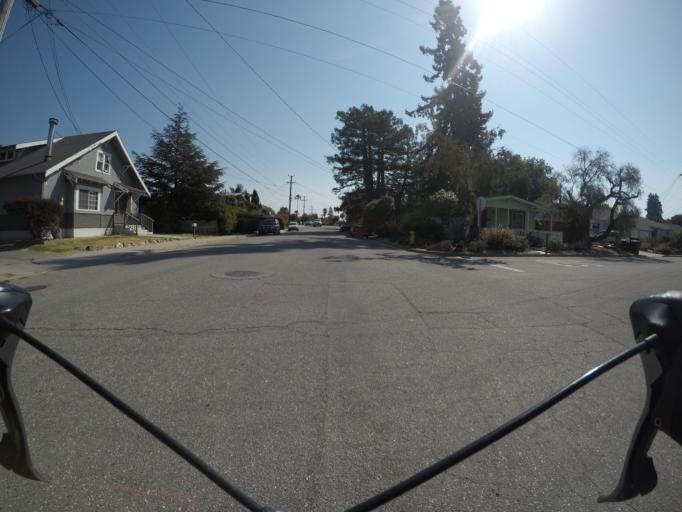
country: US
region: California
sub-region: Santa Cruz County
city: Twin Lakes
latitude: 36.9864
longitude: -122.0068
